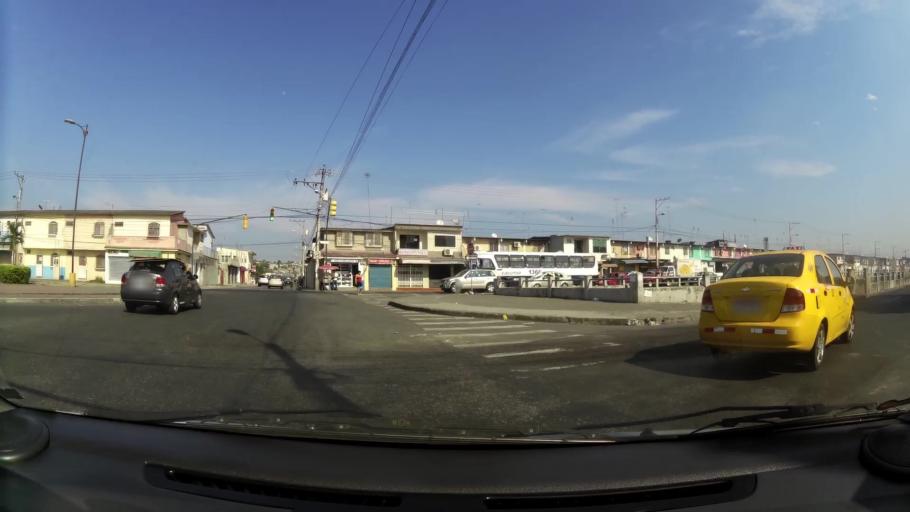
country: EC
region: Guayas
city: Eloy Alfaro
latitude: -2.0939
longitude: -79.9174
